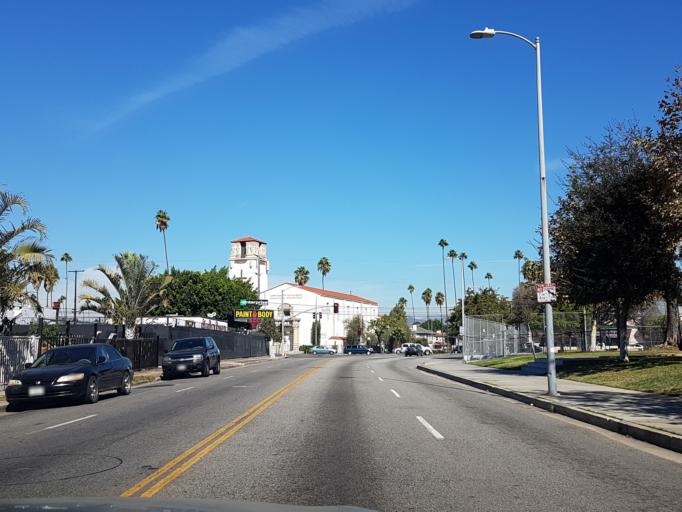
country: US
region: California
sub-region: Los Angeles County
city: Hollywood
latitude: 34.0461
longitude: -118.3177
